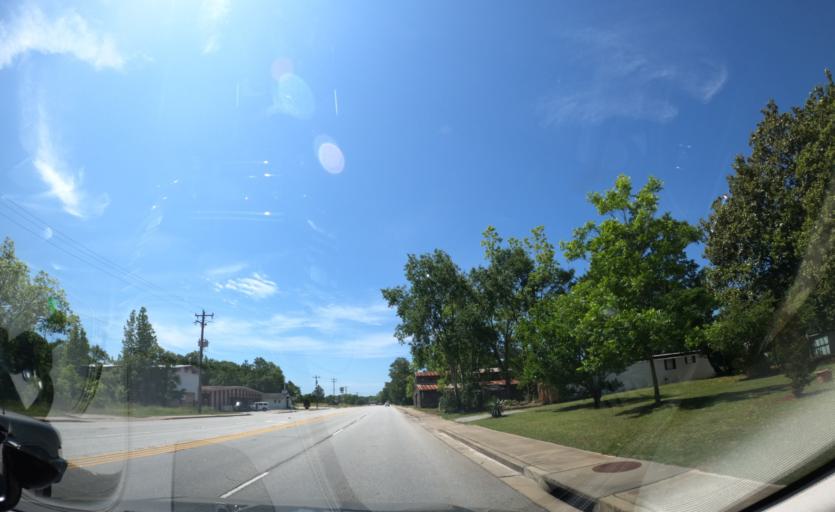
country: US
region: South Carolina
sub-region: Anderson County
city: Iva
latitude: 34.3159
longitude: -82.6634
